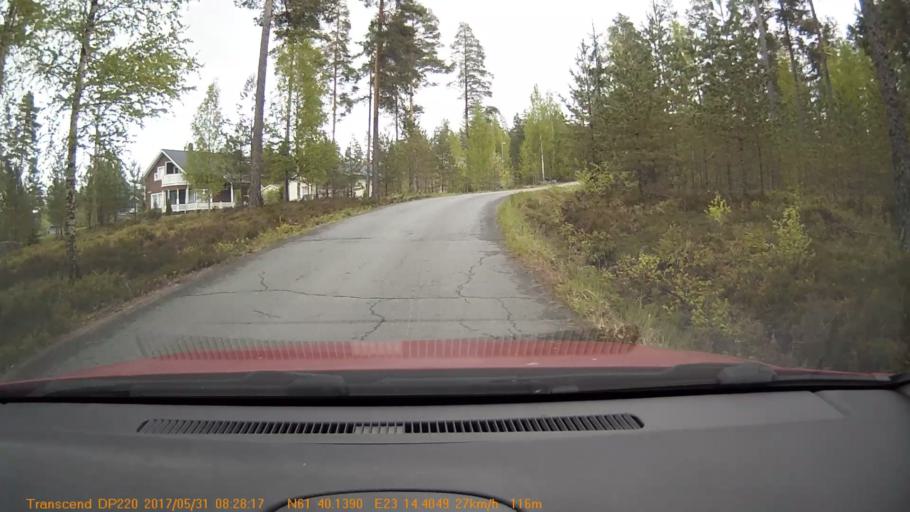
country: FI
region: Pirkanmaa
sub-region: Tampere
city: Viljakkala
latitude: 61.6690
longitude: 23.2400
